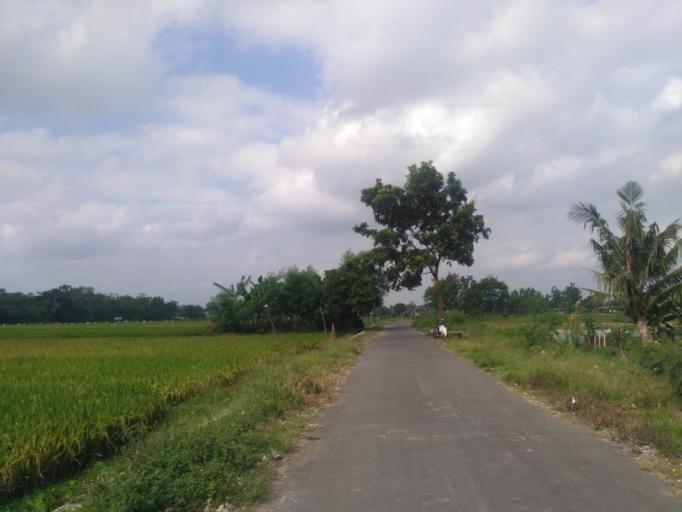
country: ID
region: Daerah Istimewa Yogyakarta
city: Yogyakarta
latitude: -7.7585
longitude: 110.3549
